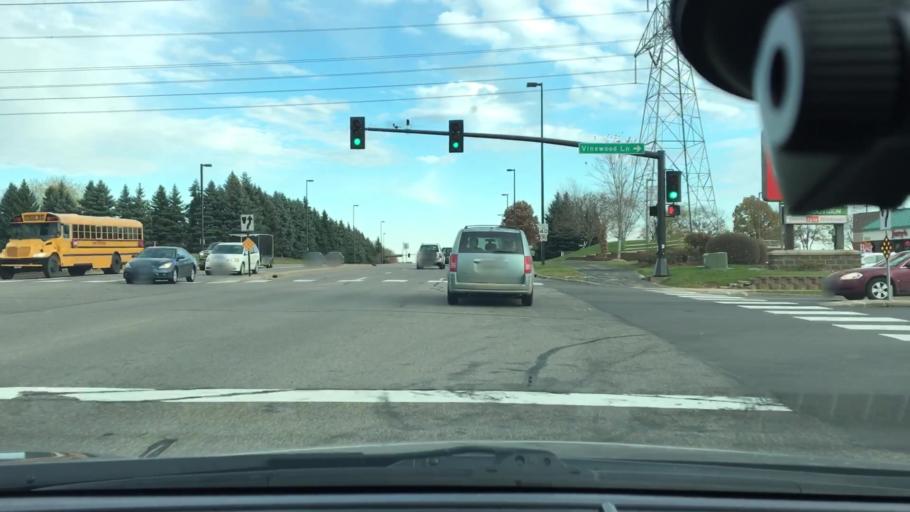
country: US
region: Minnesota
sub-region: Hennepin County
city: Maple Grove
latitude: 45.1045
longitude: -93.4481
